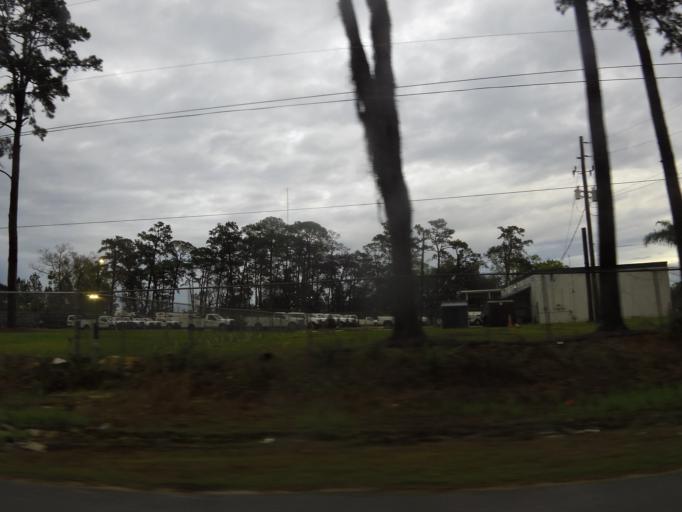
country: US
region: Florida
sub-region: Duval County
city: Jacksonville
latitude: 30.3280
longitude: -81.6989
